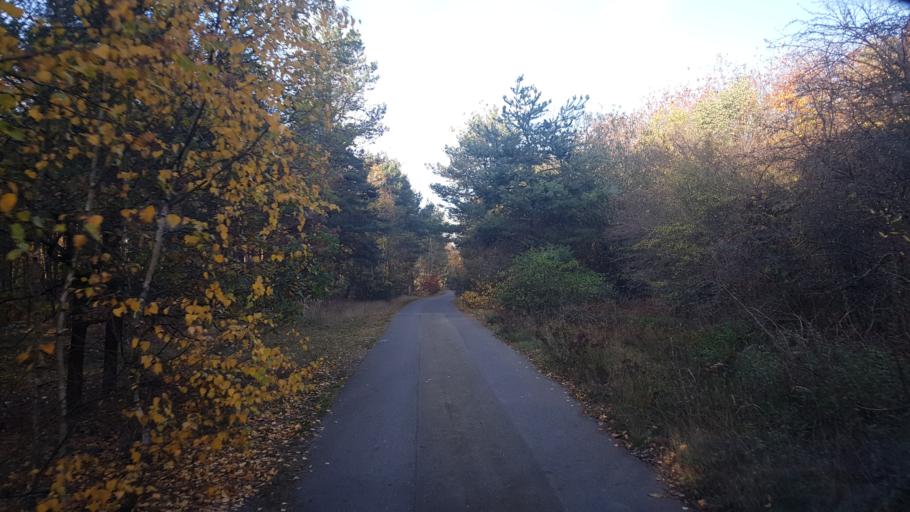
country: DE
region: Brandenburg
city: Calau
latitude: 51.7090
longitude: 13.9491
